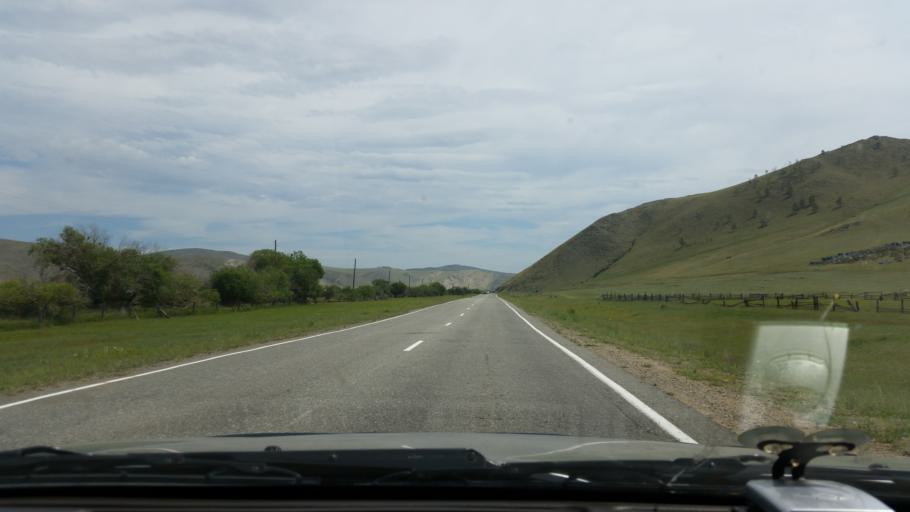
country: RU
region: Irkutsk
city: Yelantsy
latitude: 52.8060
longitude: 106.4513
